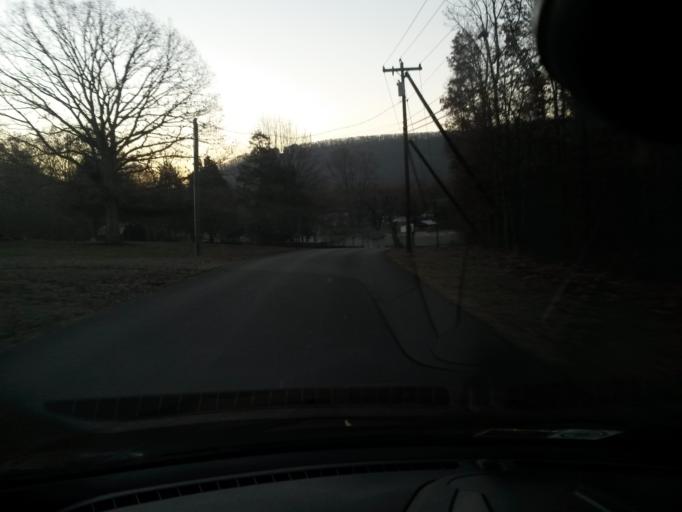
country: US
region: Virginia
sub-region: Alleghany County
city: Clifton Forge
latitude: 37.8207
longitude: -79.8118
